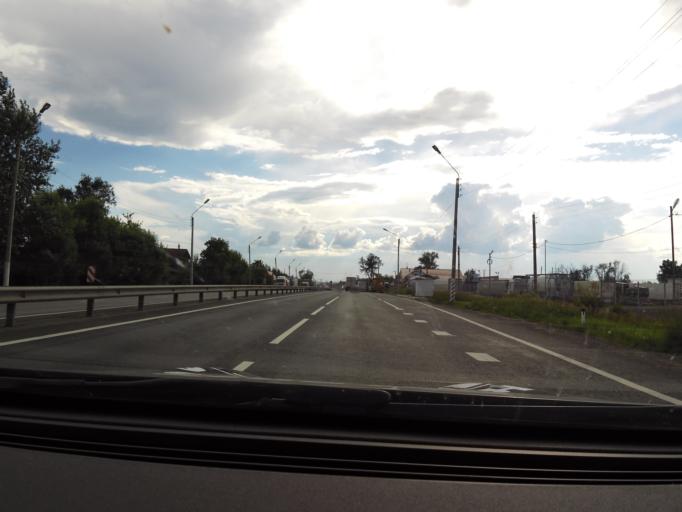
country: RU
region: Vladimir
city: Galitsy
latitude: 56.2298
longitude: 42.8012
